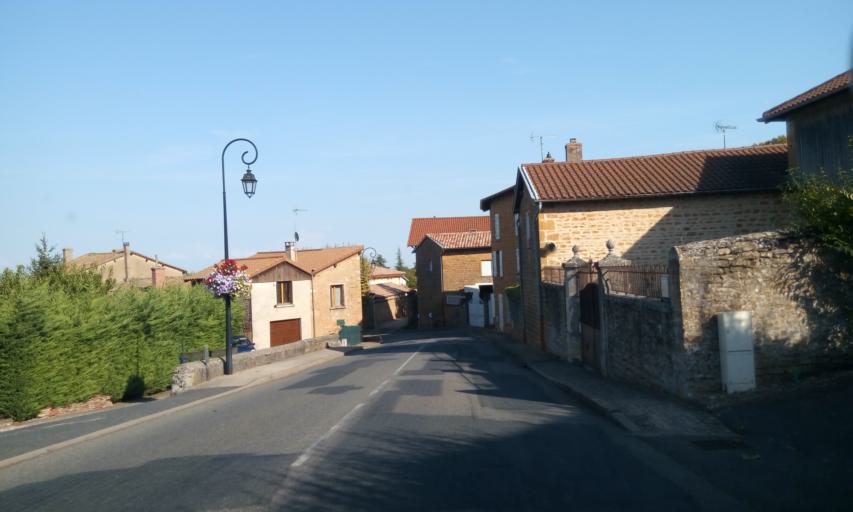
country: FR
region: Rhone-Alpes
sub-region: Departement du Rhone
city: Lucenay
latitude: 45.9252
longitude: 4.6892
